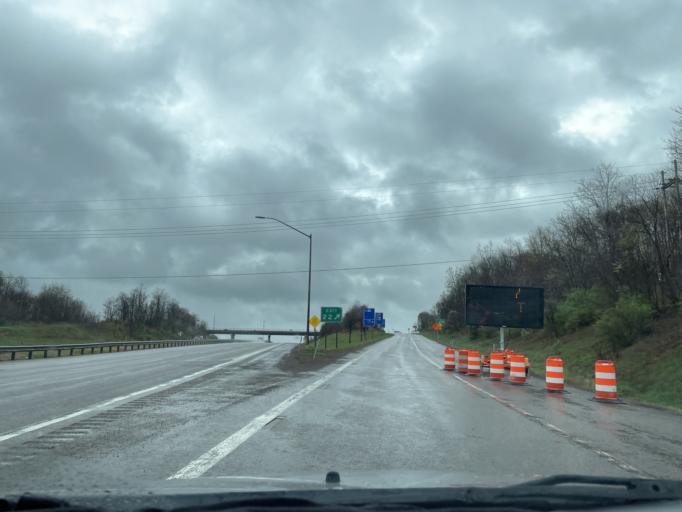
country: US
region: Pennsylvania
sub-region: Somerset County
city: Meyersdale
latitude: 39.6900
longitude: -79.1092
